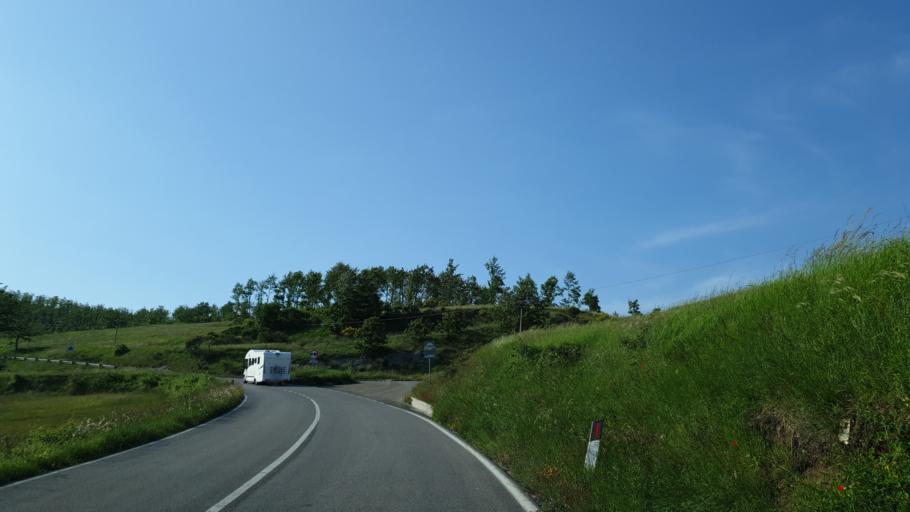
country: IT
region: Tuscany
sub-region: Province of Arezzo
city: Stia
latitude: 43.7760
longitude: 11.6855
